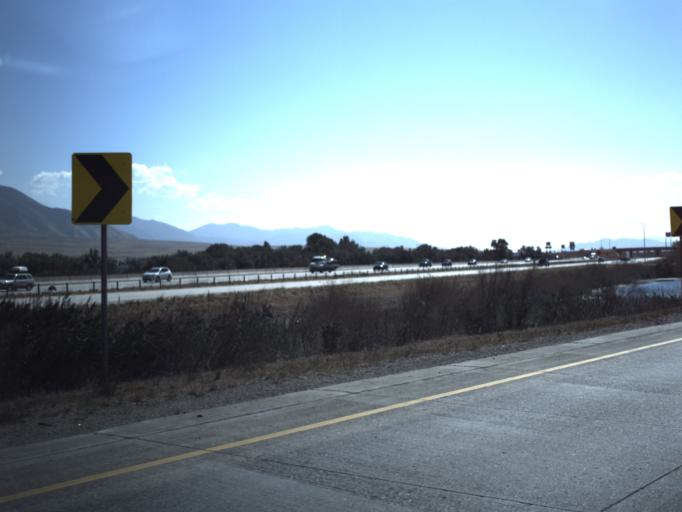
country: US
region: Utah
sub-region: Tooele County
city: Stansbury park
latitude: 40.6992
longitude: -112.2598
